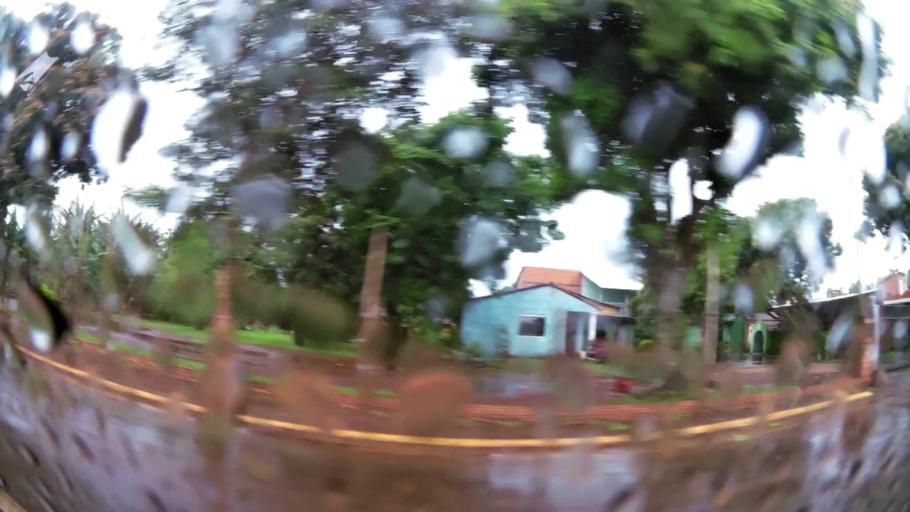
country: PY
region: Alto Parana
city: Presidente Franco
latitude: -25.5358
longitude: -54.6778
